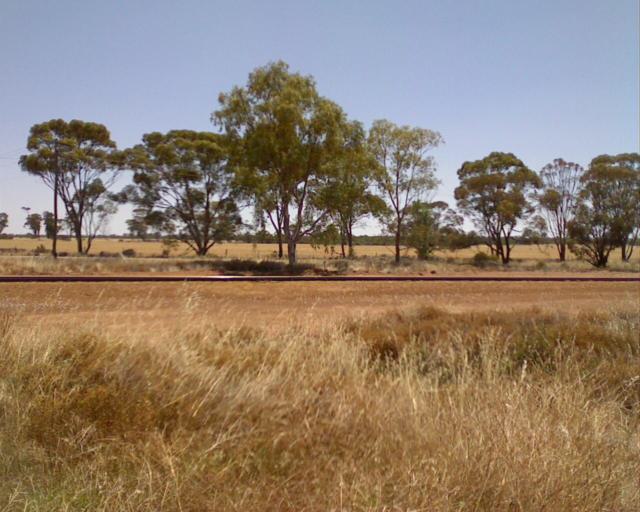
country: AU
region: Western Australia
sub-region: Wongan-Ballidu
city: Wongan Hills
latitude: -30.4540
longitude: 117.5254
